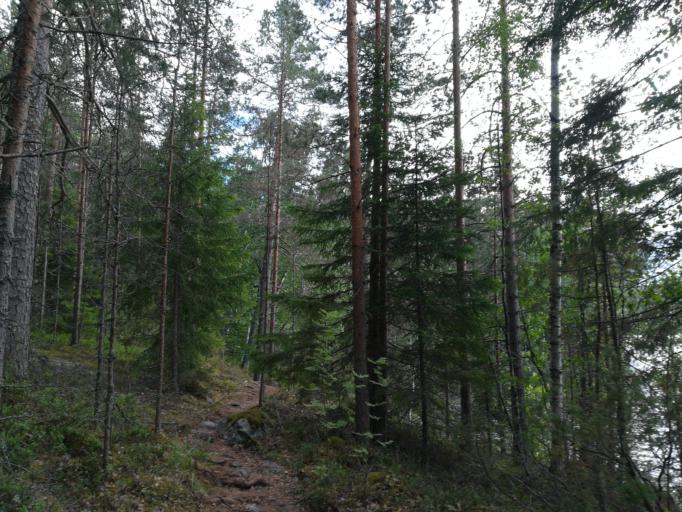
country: FI
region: South Karelia
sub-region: Lappeenranta
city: Savitaipale
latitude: 61.3053
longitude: 27.6144
